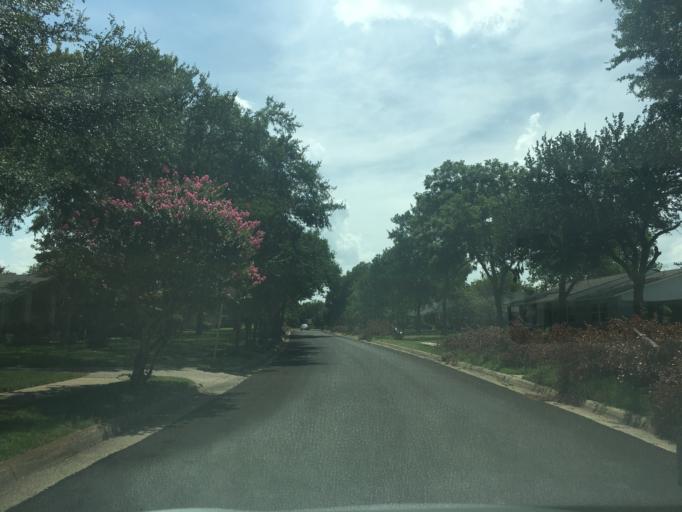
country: US
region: Texas
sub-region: Dallas County
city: Addison
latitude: 32.9162
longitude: -96.8477
